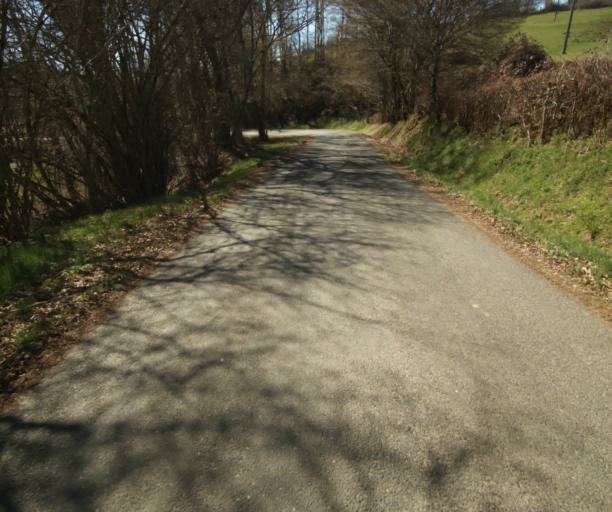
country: FR
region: Limousin
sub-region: Departement de la Correze
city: Chamboulive
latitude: 45.4518
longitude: 1.6722
